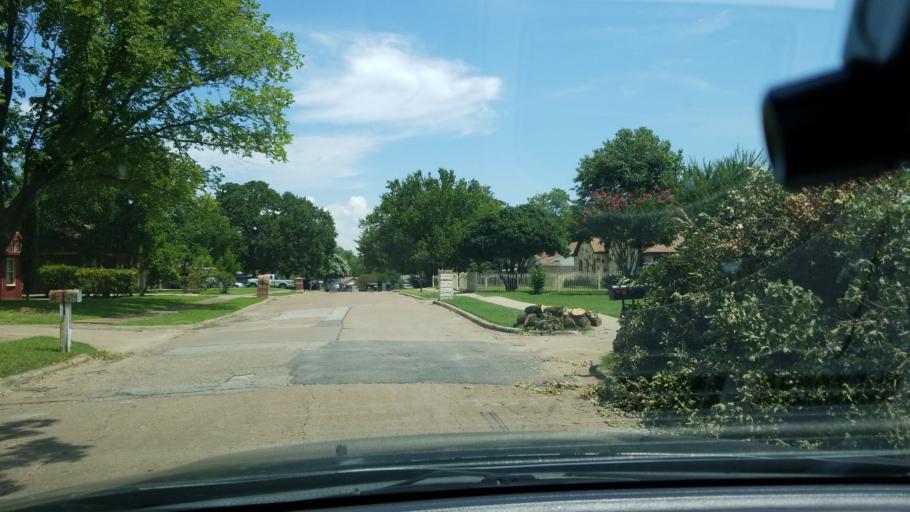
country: US
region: Texas
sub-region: Dallas County
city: Balch Springs
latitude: 32.7499
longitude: -96.6361
